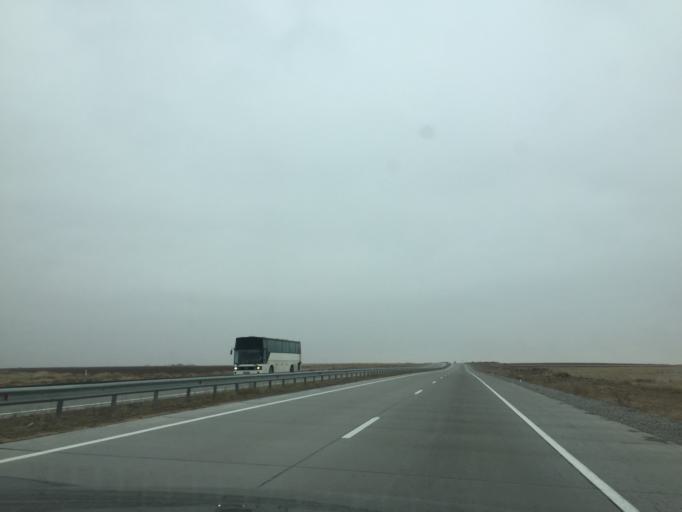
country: KZ
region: Ongtustik Qazaqstan
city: Aksu
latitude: 42.4652
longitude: 69.7785
